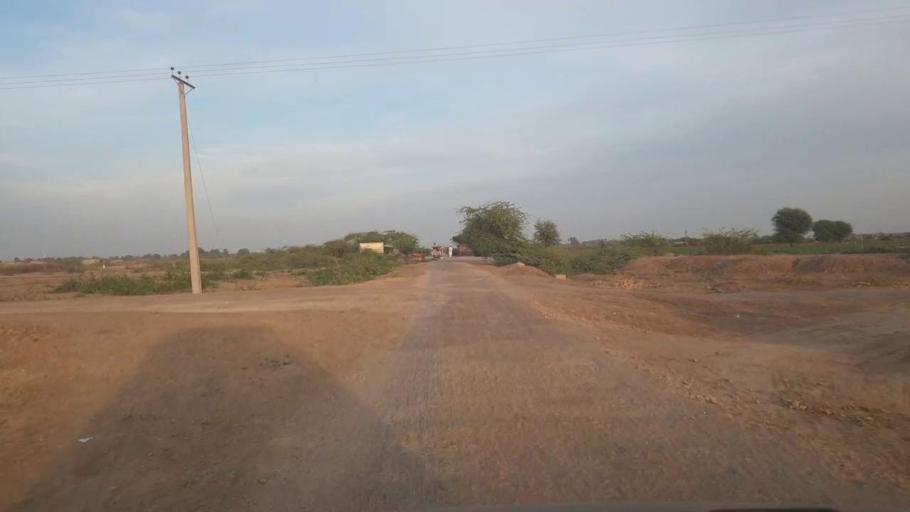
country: PK
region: Sindh
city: Kunri
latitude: 25.2122
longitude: 69.5836
